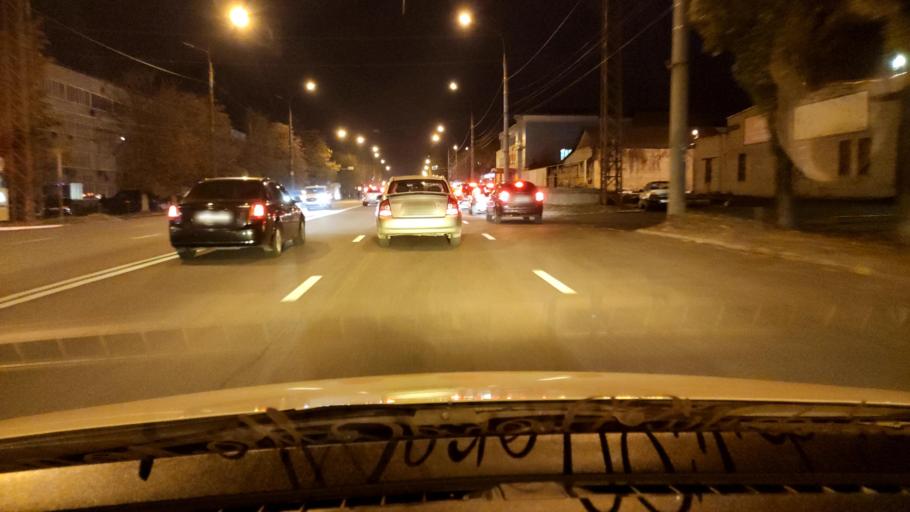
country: RU
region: Voronezj
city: Voronezh
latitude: 51.6857
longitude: 39.1657
